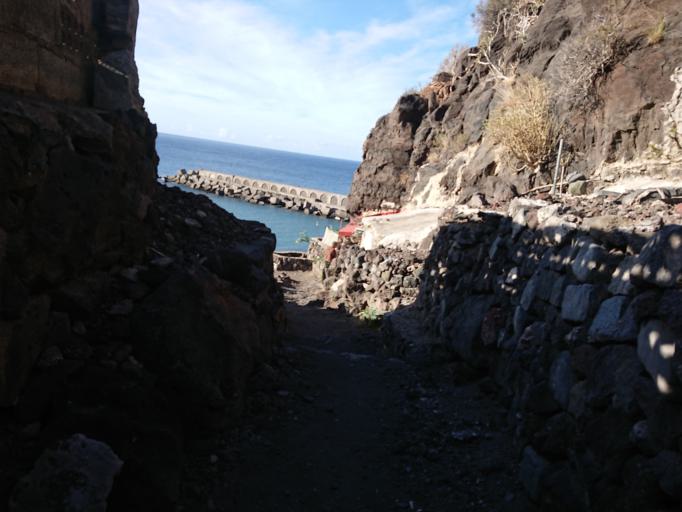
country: ES
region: Canary Islands
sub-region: Provincia de Santa Cruz de Tenerife
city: Tazacorte
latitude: 28.6524
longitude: -17.9478
